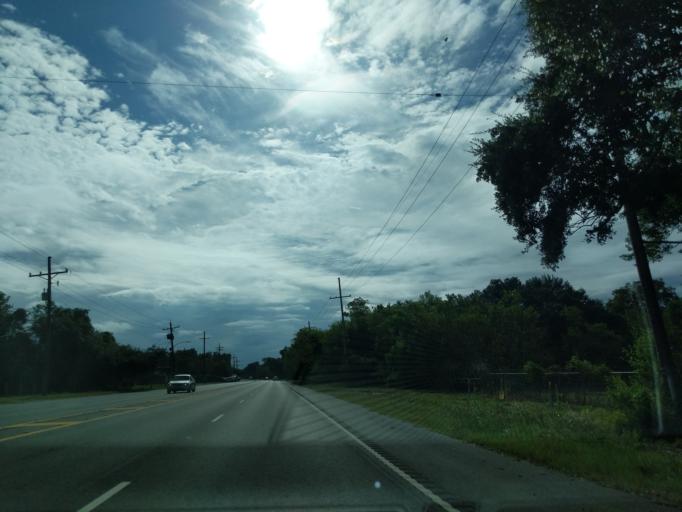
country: US
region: Louisiana
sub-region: Saint Bernard Parish
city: Chalmette
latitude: 30.0479
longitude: -89.8875
